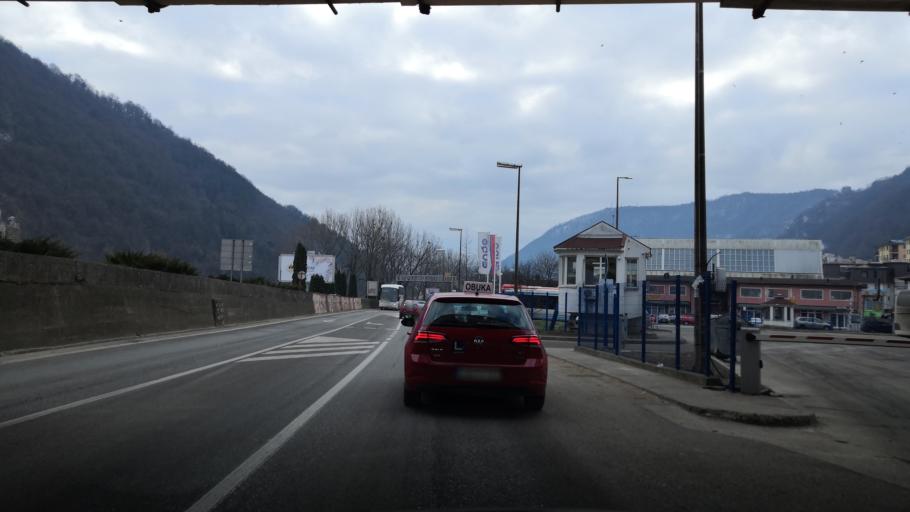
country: BA
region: Republika Srpska
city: Zvornik
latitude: 44.3856
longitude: 19.1052
